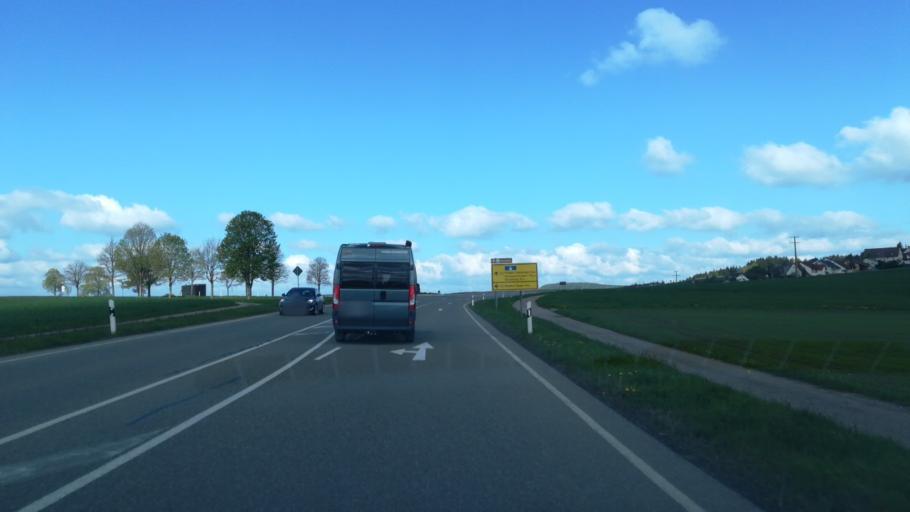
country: DE
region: Baden-Wuerttemberg
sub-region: Freiburg Region
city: Blumberg
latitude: 47.8159
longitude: 8.5826
